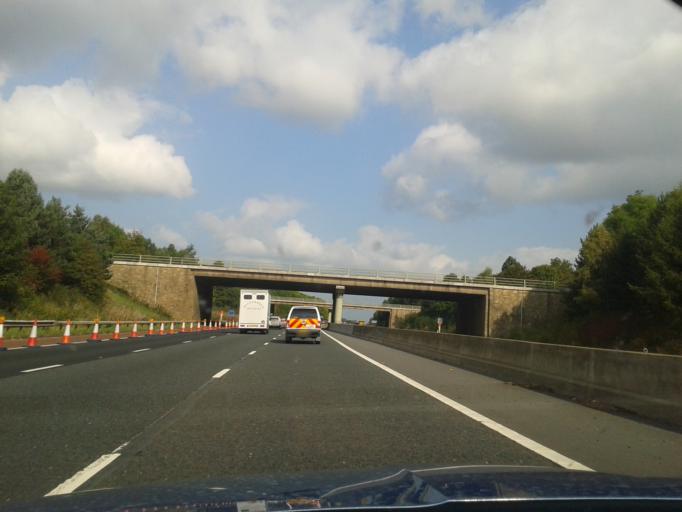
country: GB
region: England
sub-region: Cumbria
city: Penrith
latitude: 54.6921
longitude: -2.7917
